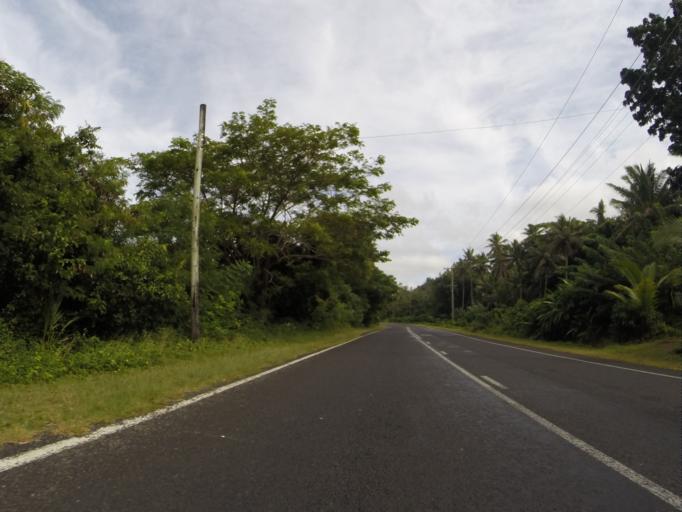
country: FJ
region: Western
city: Nadi
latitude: -18.2016
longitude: 177.6825
